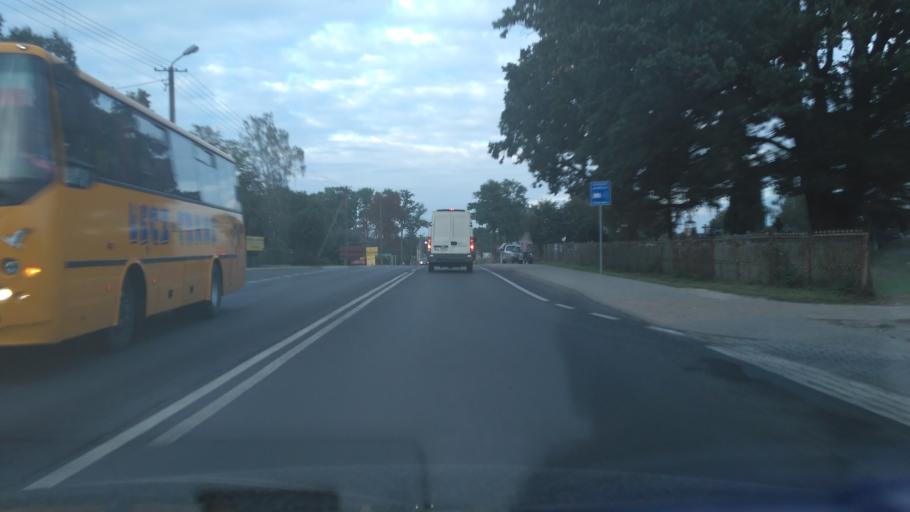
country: PL
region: Lublin Voivodeship
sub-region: Powiat leczynski
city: Spiczyn
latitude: 51.3006
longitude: 22.7244
